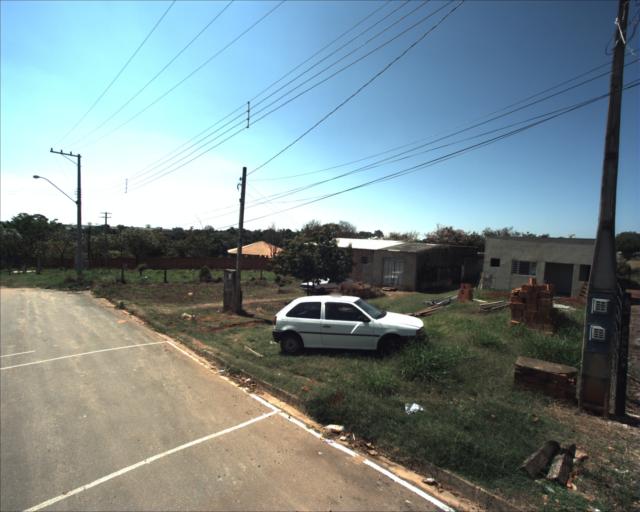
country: BR
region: Sao Paulo
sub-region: Sorocaba
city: Sorocaba
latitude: -23.4405
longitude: -47.5361
